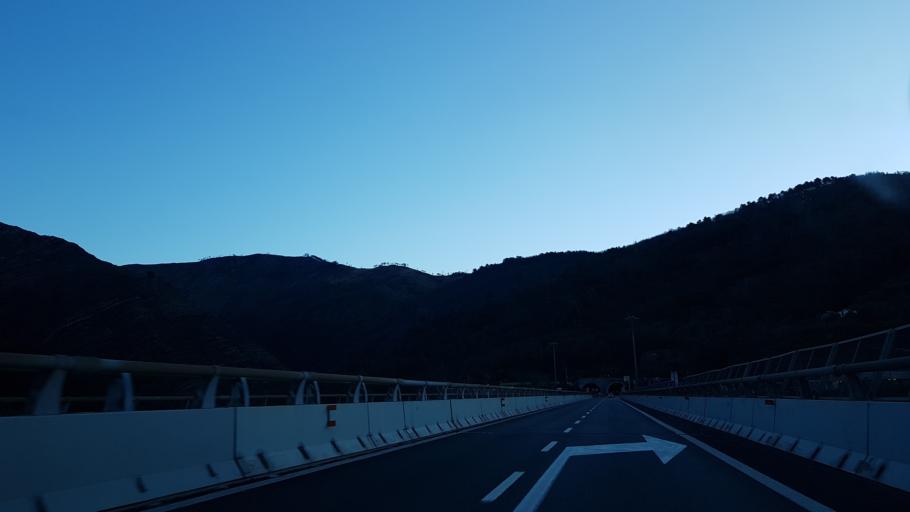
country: IT
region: Liguria
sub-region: Provincia di Genova
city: Bogliasco
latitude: 44.3925
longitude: 9.0417
